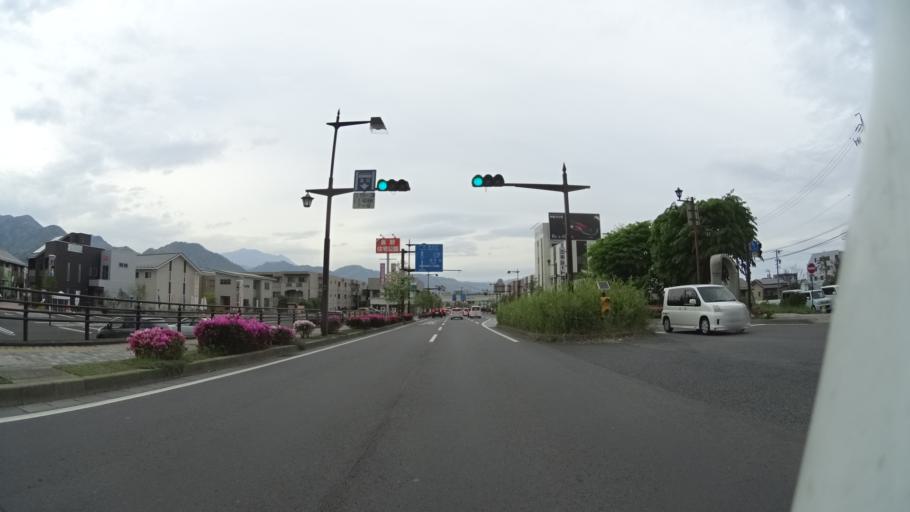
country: JP
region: Nagano
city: Nagano-shi
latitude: 36.6265
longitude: 138.1828
